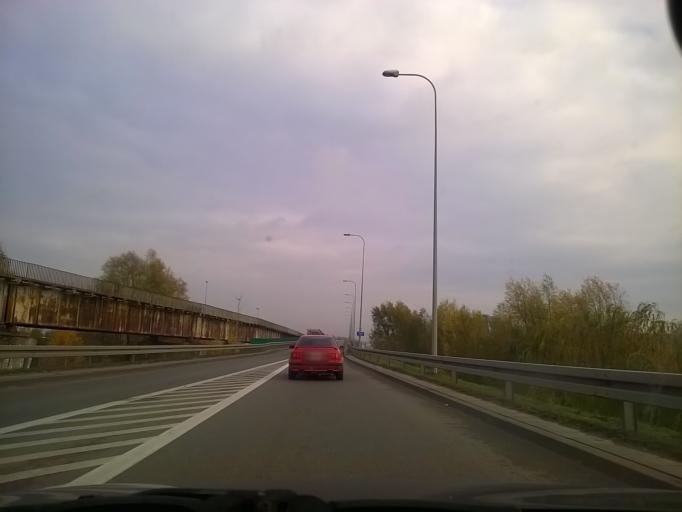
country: PL
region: Warmian-Masurian Voivodeship
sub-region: Powiat elblaski
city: Elblag
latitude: 54.1711
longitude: 19.3841
